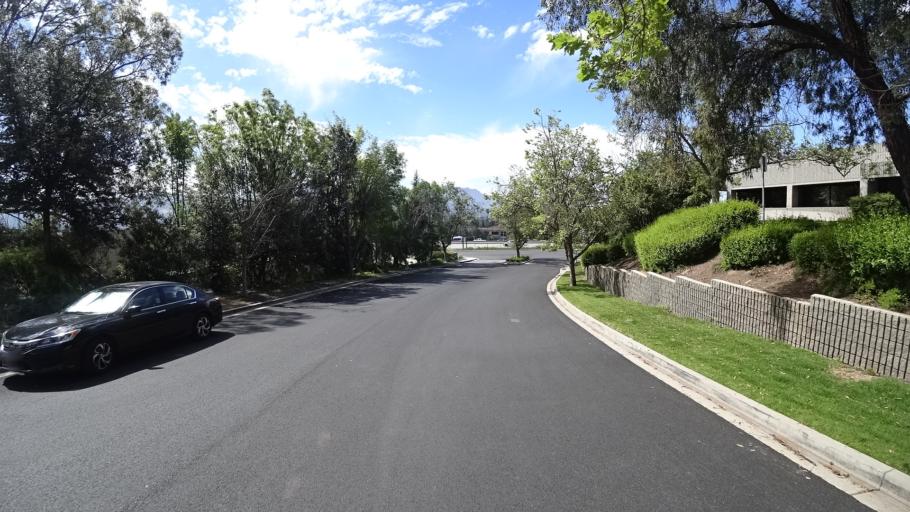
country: US
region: California
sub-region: Ventura County
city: Casa Conejo
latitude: 34.1925
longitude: -118.9427
